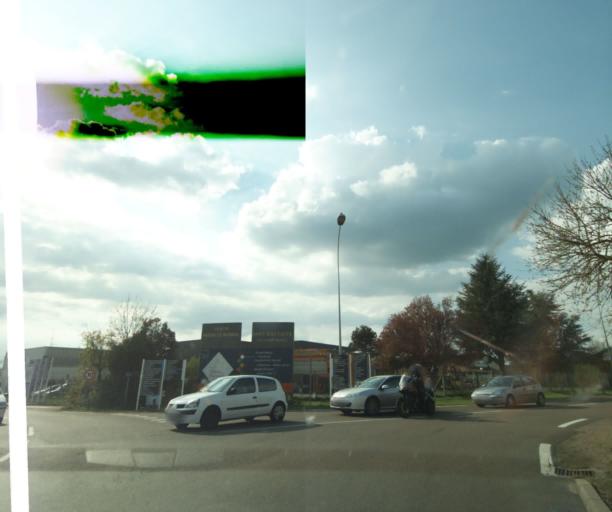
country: FR
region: Bourgogne
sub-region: Departement de Saone-et-Loire
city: Paray-le-Monial
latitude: 46.4659
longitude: 4.1176
